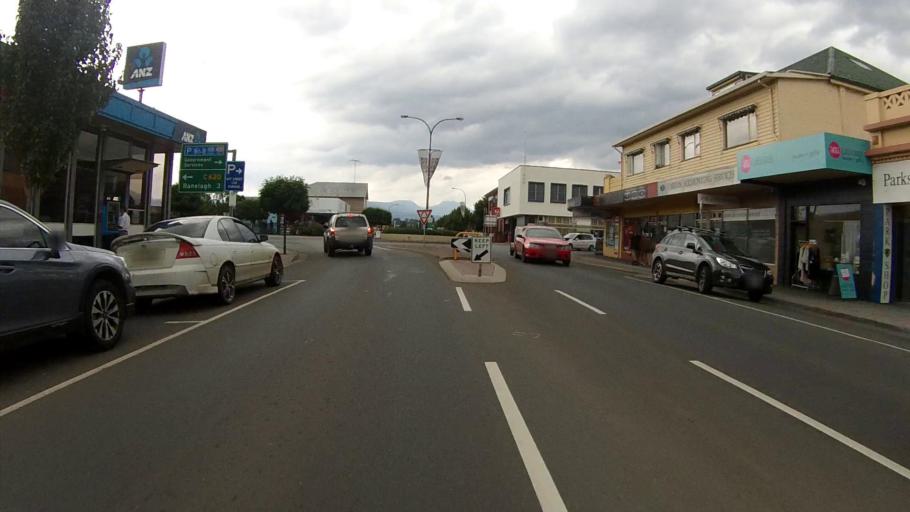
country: AU
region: Tasmania
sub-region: Huon Valley
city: Huonville
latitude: -43.0313
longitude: 147.0481
